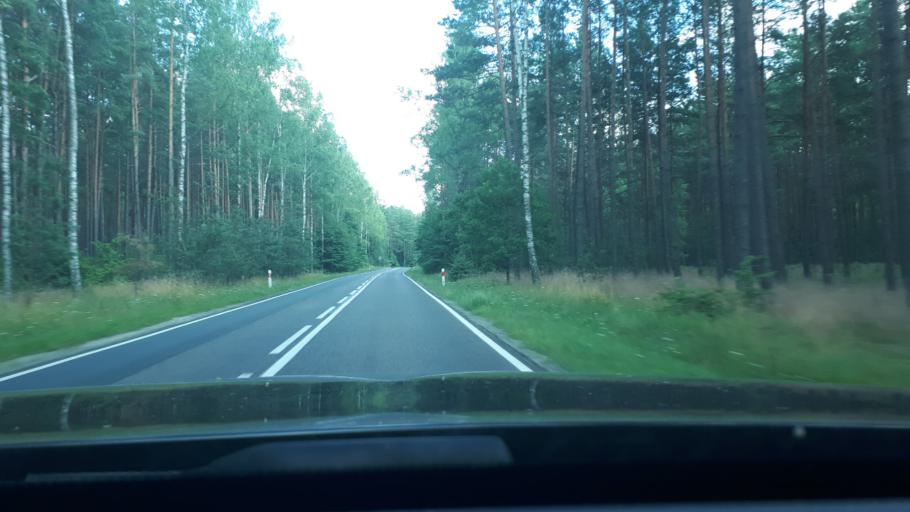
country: PL
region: Warmian-Masurian Voivodeship
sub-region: Powiat olsztynski
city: Stawiguda
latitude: 53.5313
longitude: 20.4384
